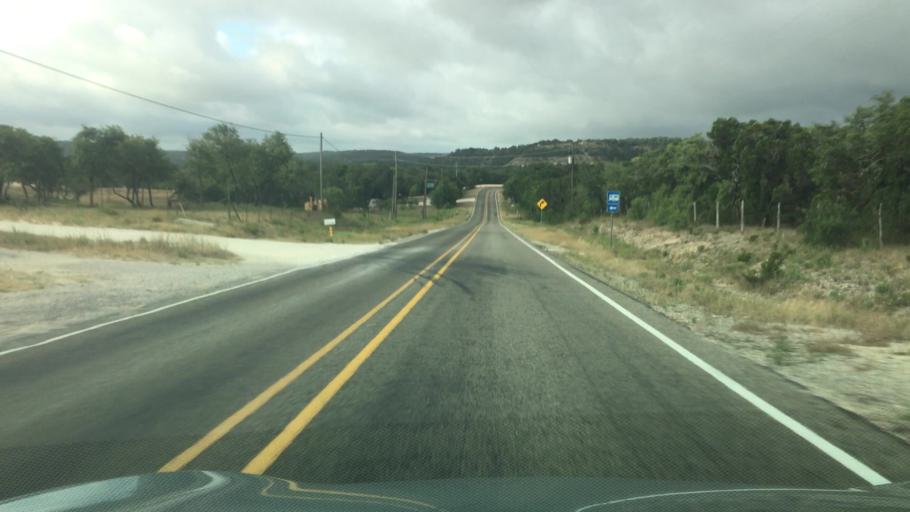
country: US
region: Texas
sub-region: Hays County
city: Dripping Springs
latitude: 30.1652
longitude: -98.2458
